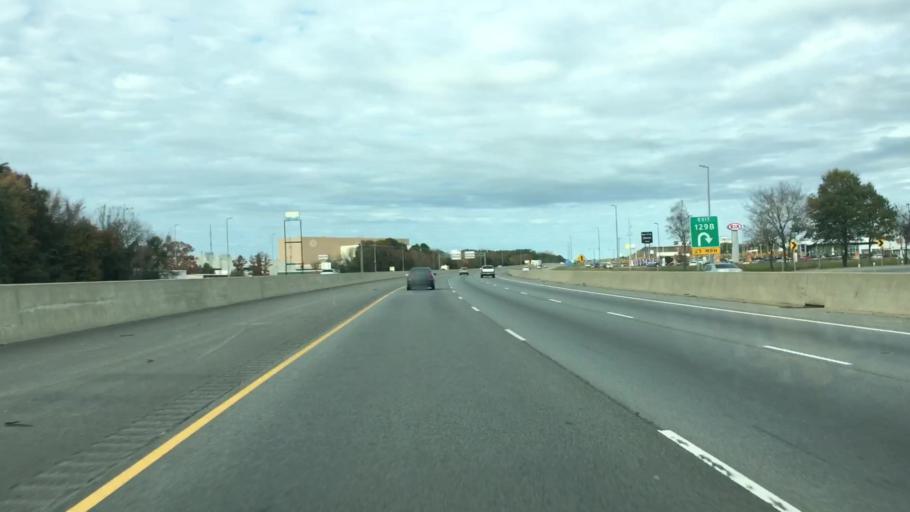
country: US
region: Arkansas
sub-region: Faulkner County
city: Conway
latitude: 35.0671
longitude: -92.4178
